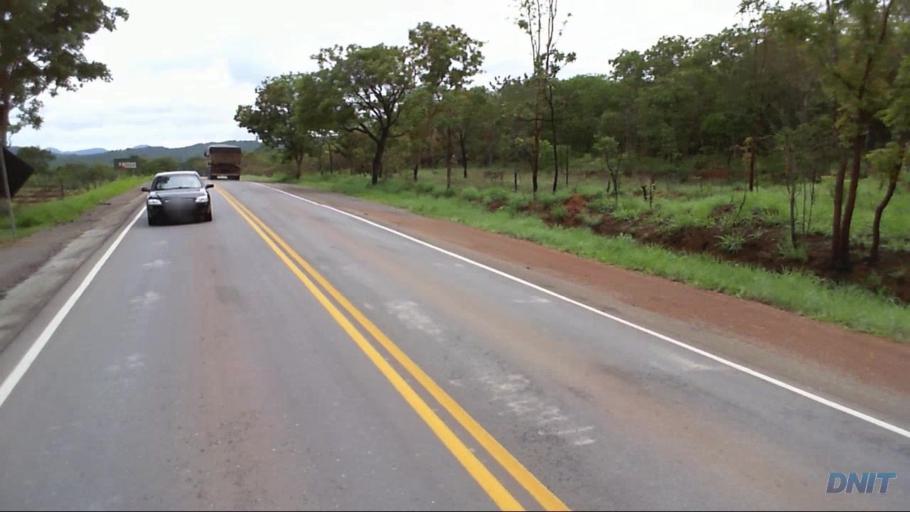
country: BR
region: Goias
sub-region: Padre Bernardo
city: Padre Bernardo
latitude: -15.4556
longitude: -48.2139
